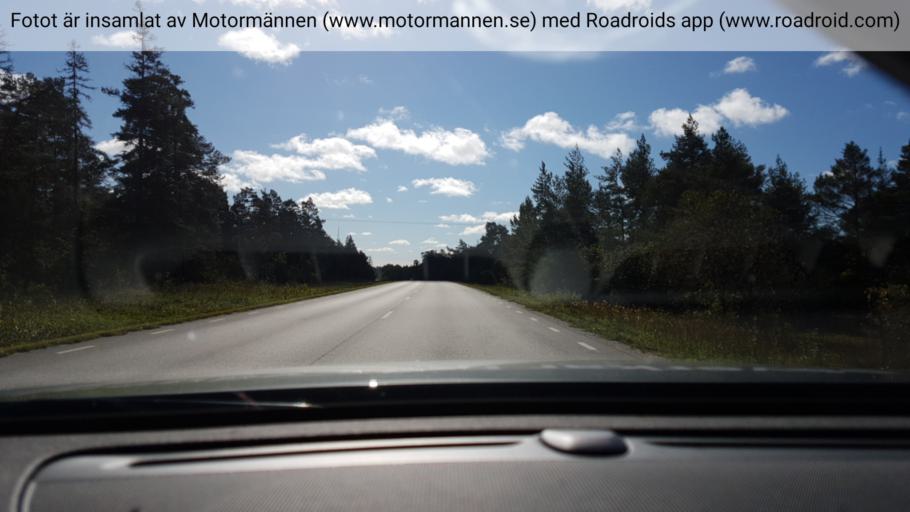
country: SE
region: Gotland
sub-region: Gotland
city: Slite
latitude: 57.7470
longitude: 18.7894
